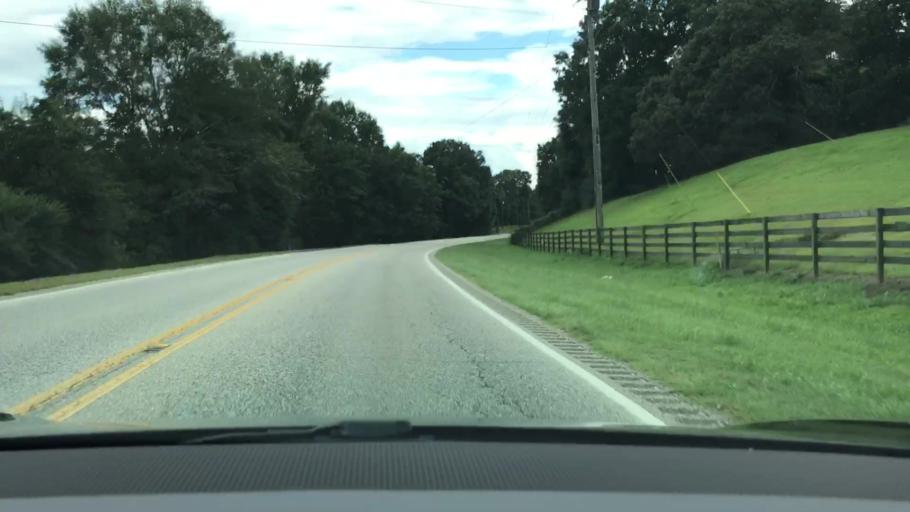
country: US
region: Alabama
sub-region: Pike County
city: Troy
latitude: 31.7402
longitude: -85.9573
